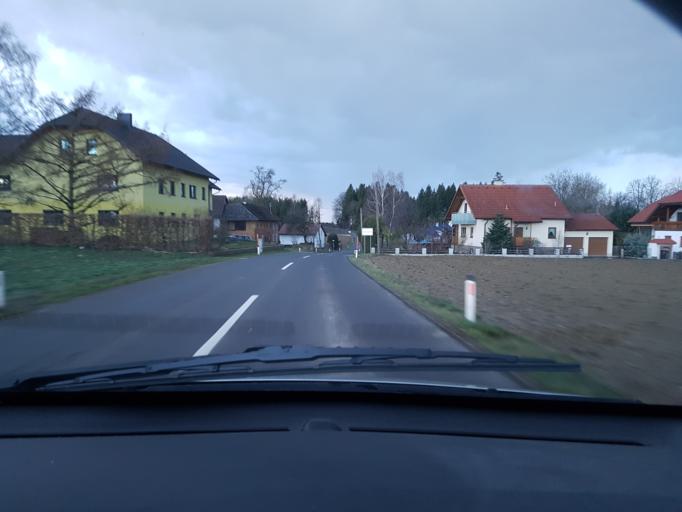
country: AT
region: Upper Austria
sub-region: Politischer Bezirk Linz-Land
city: Ansfelden
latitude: 48.1637
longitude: 14.3233
